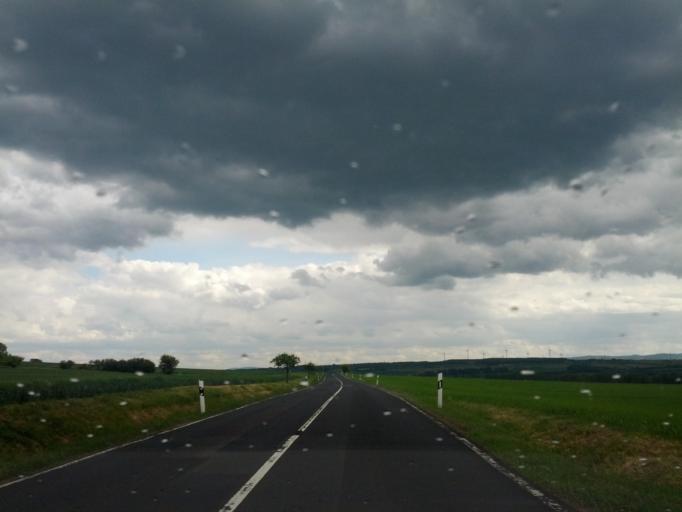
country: DE
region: Thuringia
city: Friedrichswerth
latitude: 51.0143
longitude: 10.5337
